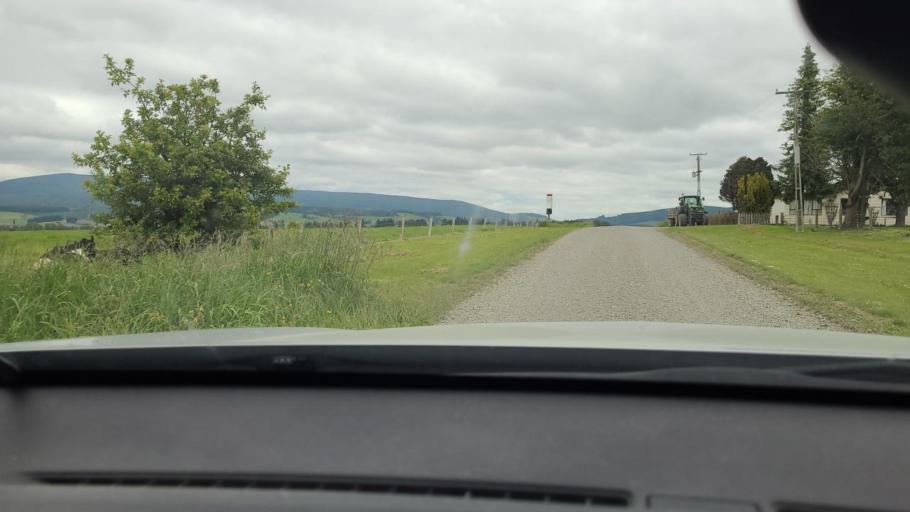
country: NZ
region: Southland
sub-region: Southland District
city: Riverton
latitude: -46.0831
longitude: 167.9743
